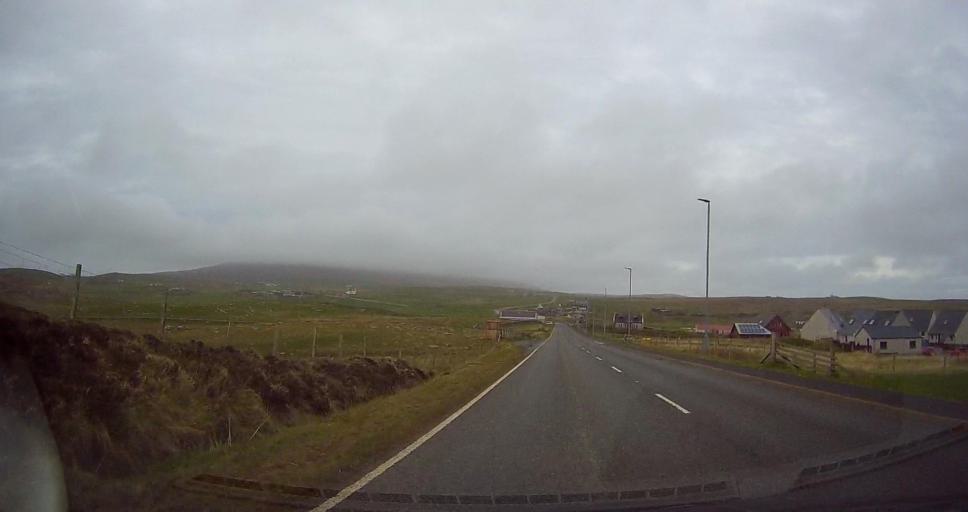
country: GB
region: Scotland
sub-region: Shetland Islands
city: Sandwick
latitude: 59.9214
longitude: -1.2993
